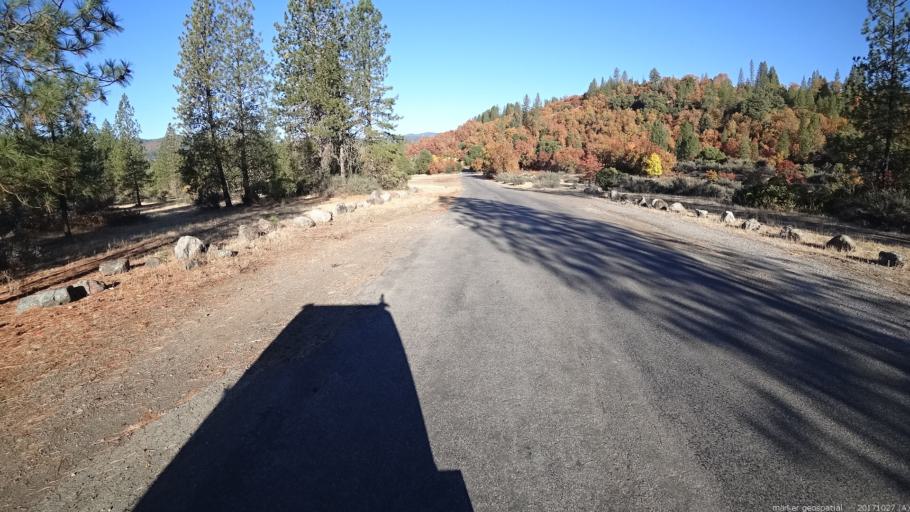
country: US
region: California
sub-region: Shasta County
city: Burney
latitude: 41.0218
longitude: -121.9110
